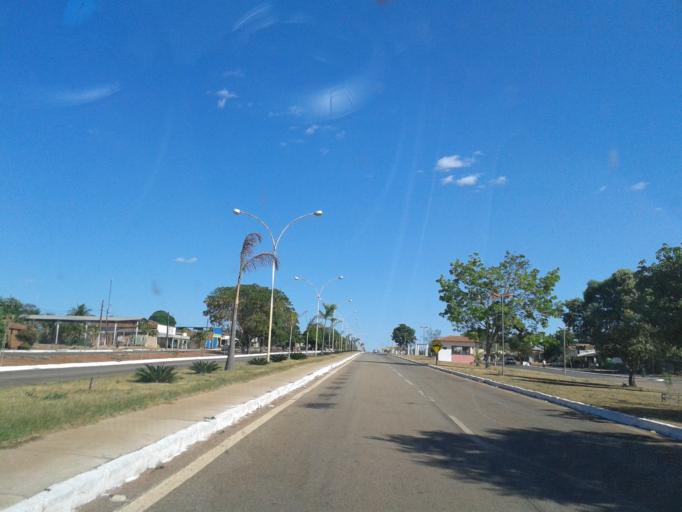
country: BR
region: Goias
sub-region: Crixas
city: Crixas
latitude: -14.0901
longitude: -50.3359
